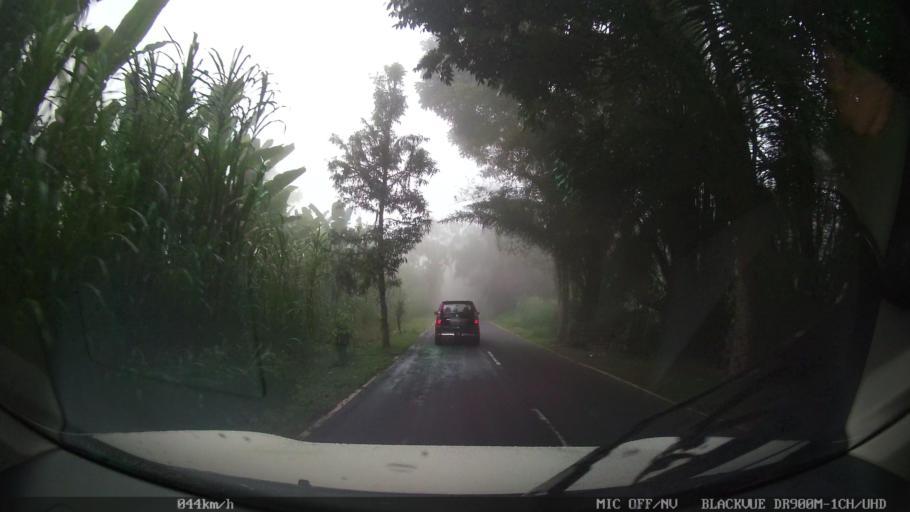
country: ID
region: Bali
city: Banjar Taro Kelod
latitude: -8.3439
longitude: 115.2801
